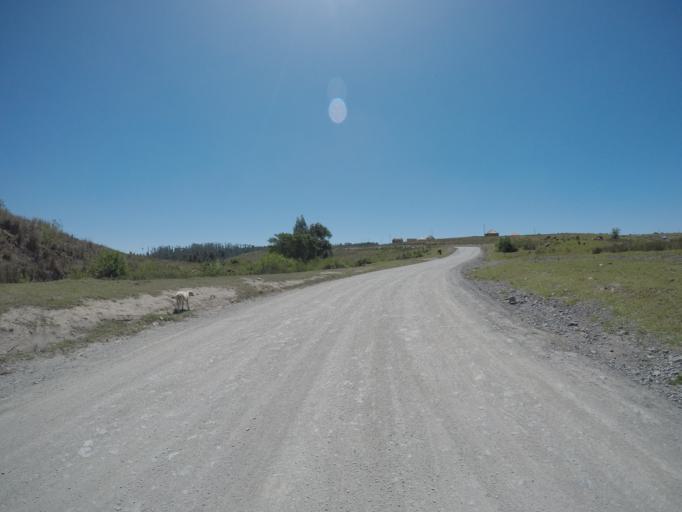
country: ZA
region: Eastern Cape
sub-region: OR Tambo District Municipality
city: Libode
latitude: -31.9671
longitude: 29.0246
